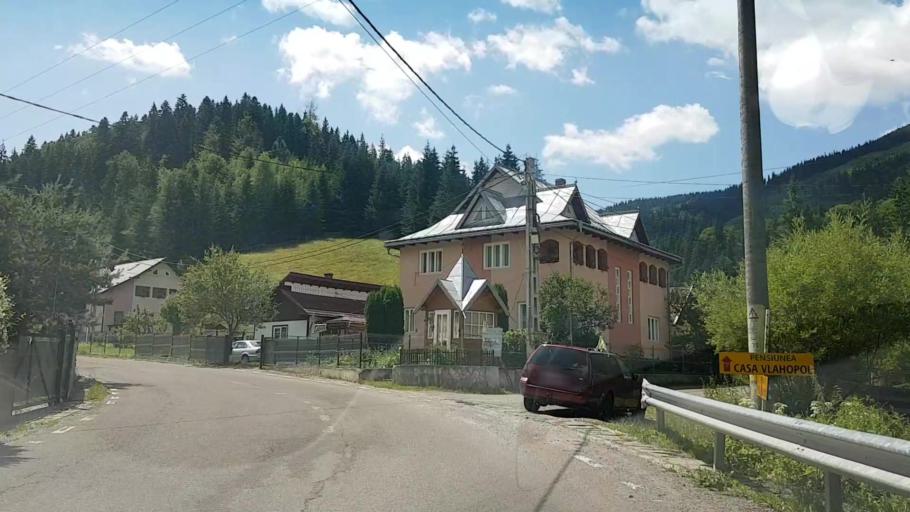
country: RO
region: Suceava
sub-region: Comuna Sadova
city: Sadova
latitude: 47.4825
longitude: 25.4917
